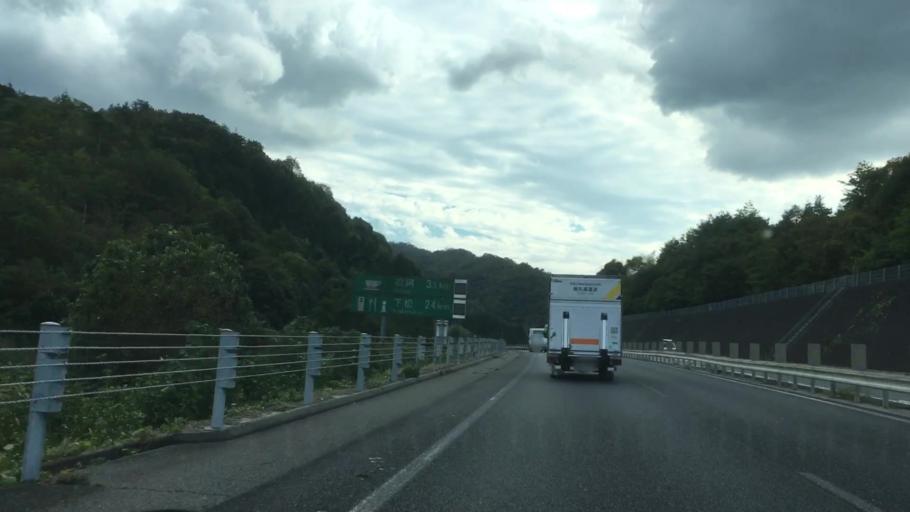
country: JP
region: Yamaguchi
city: Iwakuni
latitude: 34.1271
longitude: 132.1112
